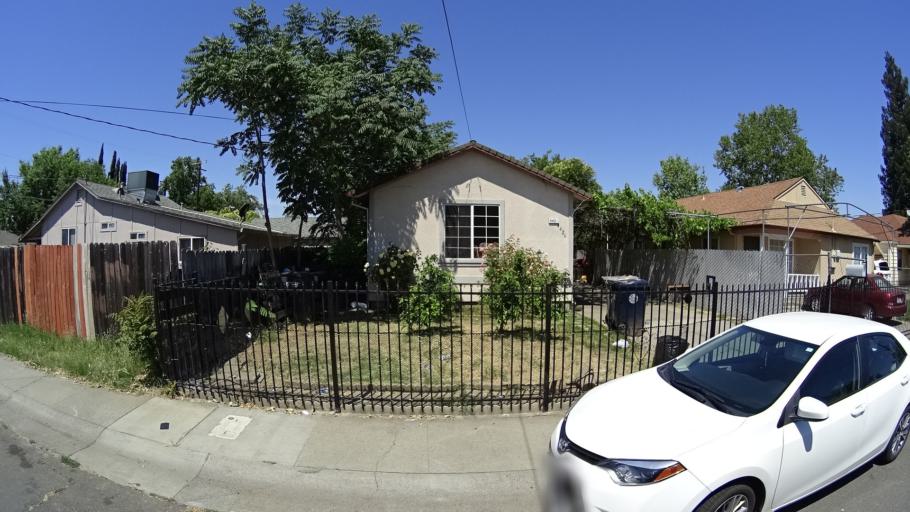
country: US
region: California
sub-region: Sacramento County
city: Florin
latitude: 38.5344
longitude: -121.4162
